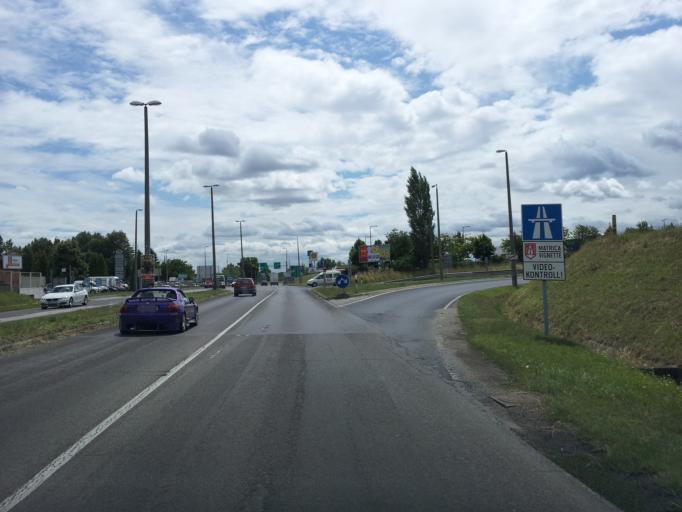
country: HU
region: Somogy
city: Siofok
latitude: 46.8949
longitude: 18.0566
